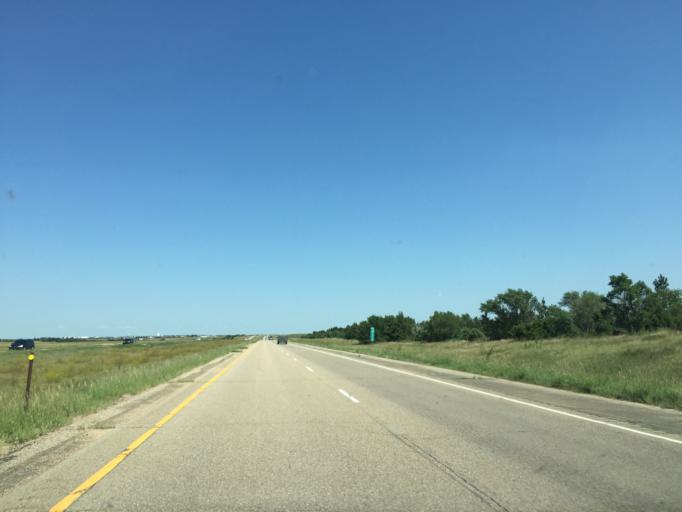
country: US
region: Colorado
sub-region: Kit Carson County
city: Burlington
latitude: 39.2941
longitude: -102.3691
